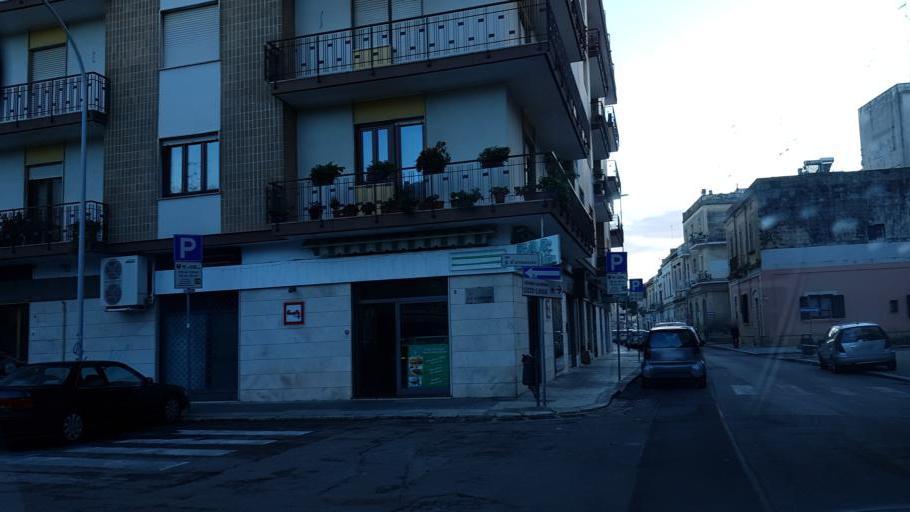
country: IT
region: Apulia
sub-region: Provincia di Lecce
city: Lecce
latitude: 40.3603
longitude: 18.1756
